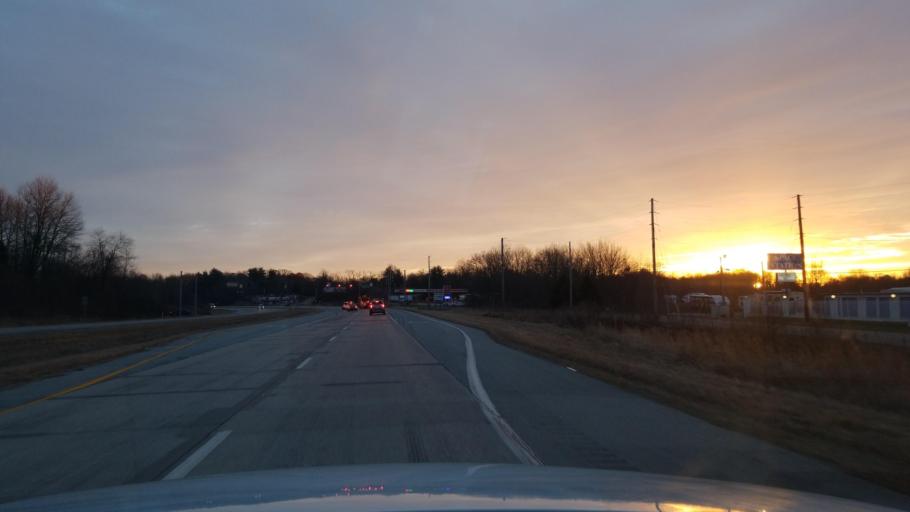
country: US
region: Indiana
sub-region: Vanderburgh County
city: Evansville
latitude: 37.9423
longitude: -87.7212
